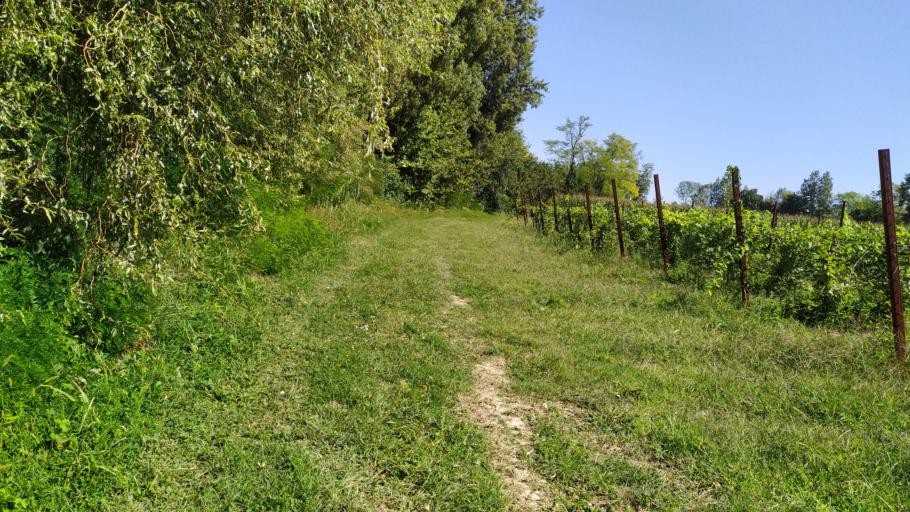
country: IT
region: Friuli Venezia Giulia
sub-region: Provincia di Pordenone
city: Cavolano-Schiavoi
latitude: 45.9401
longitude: 12.5020
